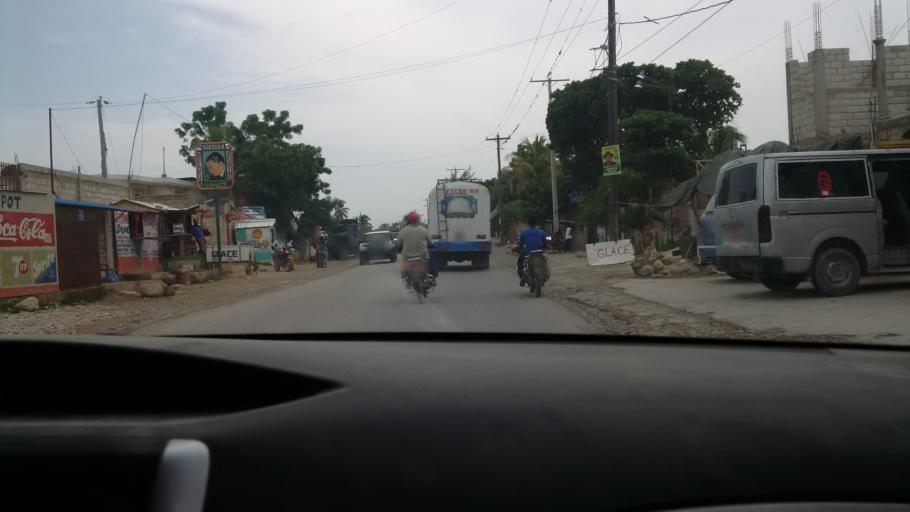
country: HT
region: Ouest
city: Gressier
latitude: 18.5426
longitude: -72.5224
